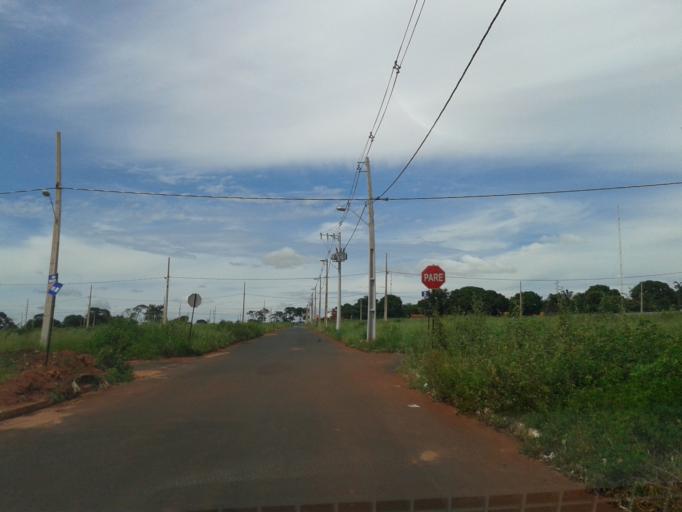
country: BR
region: Minas Gerais
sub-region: Santa Vitoria
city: Santa Vitoria
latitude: -18.8327
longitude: -50.1395
